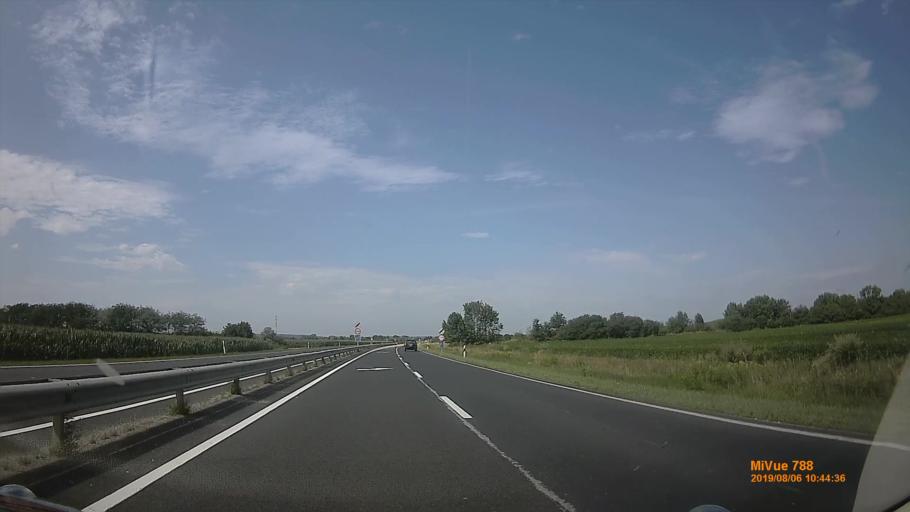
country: AT
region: Burgenland
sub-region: Politischer Bezirk Gussing
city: Heiligenbrunn
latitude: 46.9697
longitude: 16.4715
